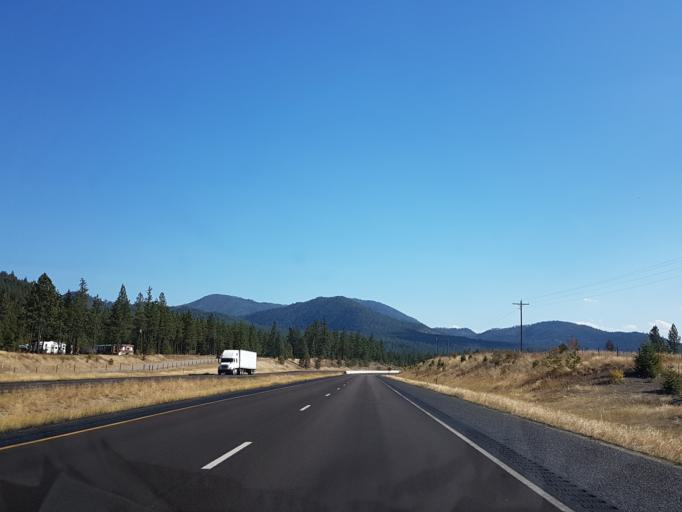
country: US
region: Montana
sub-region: Mineral County
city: Superior
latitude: 47.1360
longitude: -114.8023
